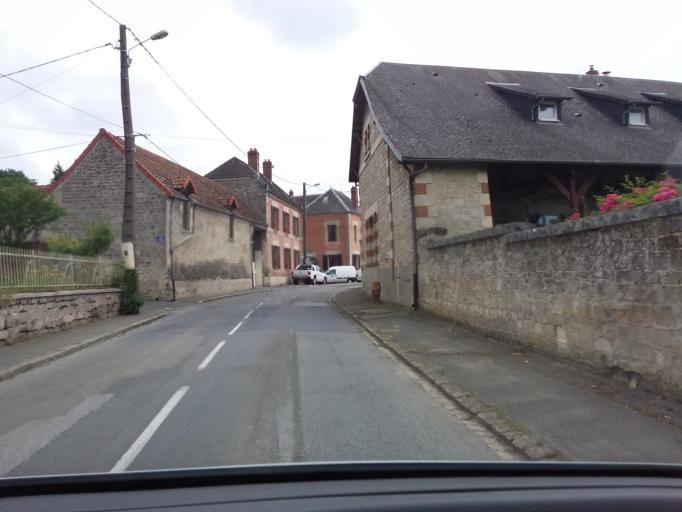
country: FR
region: Picardie
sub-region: Departement de l'Aisne
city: Vailly-sur-Aisne
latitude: 49.3972
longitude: 3.4668
